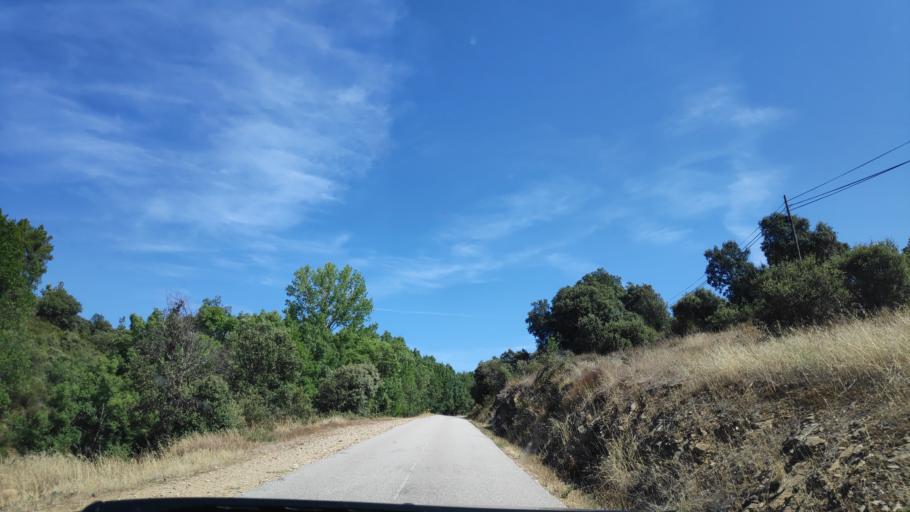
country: ES
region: Castille and Leon
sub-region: Provincia de Zamora
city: Trabazos
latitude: 41.7410
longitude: -6.5783
